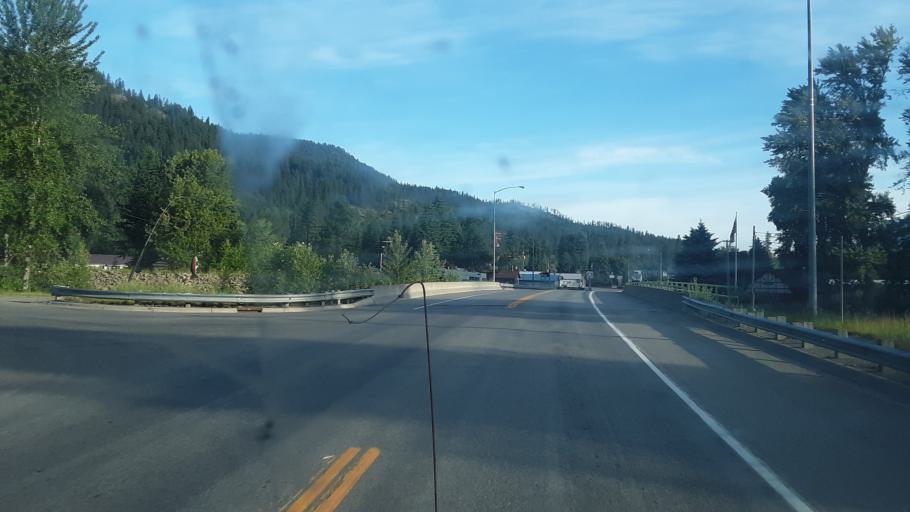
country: US
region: Montana
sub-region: Lincoln County
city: Libby
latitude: 48.4559
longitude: -115.8909
